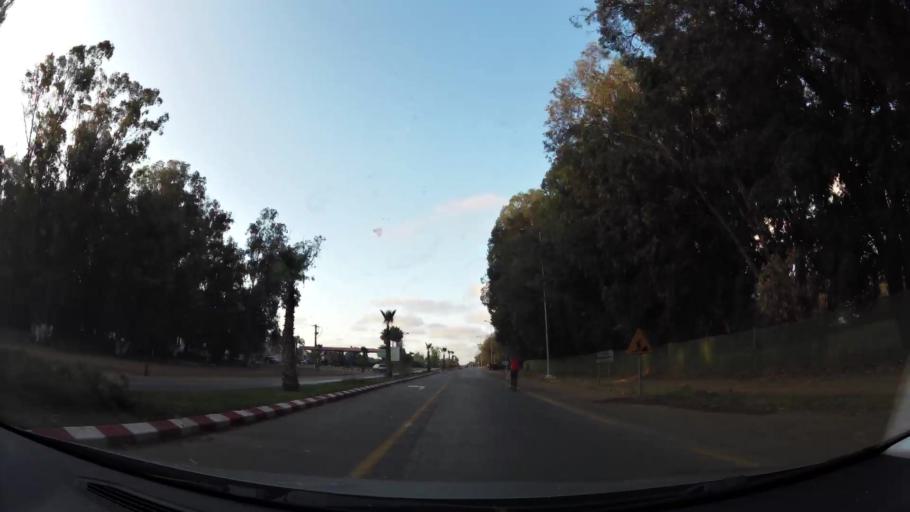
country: MA
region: Gharb-Chrarda-Beni Hssen
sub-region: Kenitra Province
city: Kenitra
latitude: 34.2027
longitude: -6.6767
